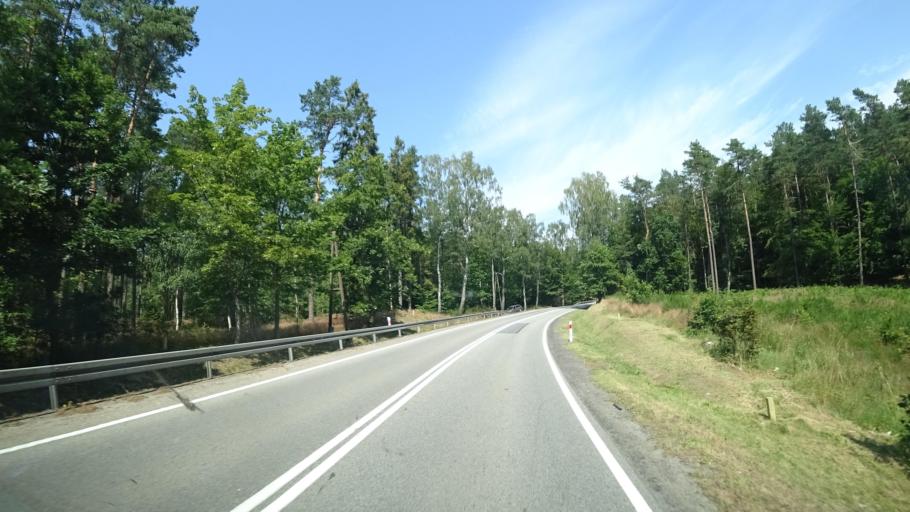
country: PL
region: Pomeranian Voivodeship
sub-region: Powiat koscierski
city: Grabowo Koscierskie
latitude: 54.2112
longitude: 18.1141
